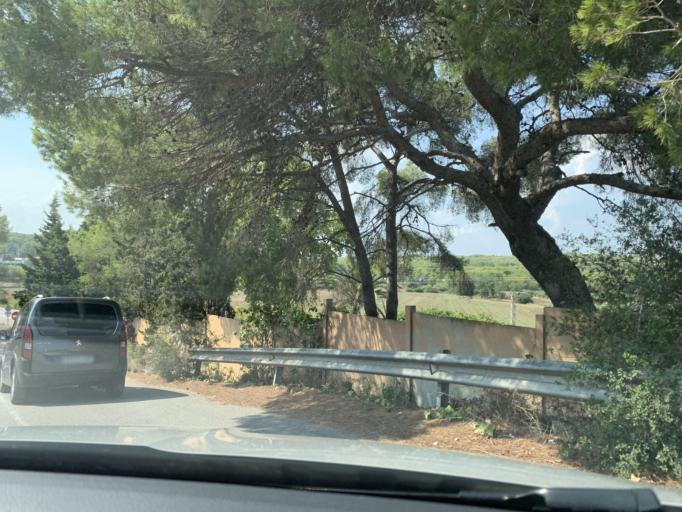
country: ES
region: Catalonia
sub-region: Provincia de Tarragona
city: Altafulla
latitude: 41.1388
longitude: 1.3532
